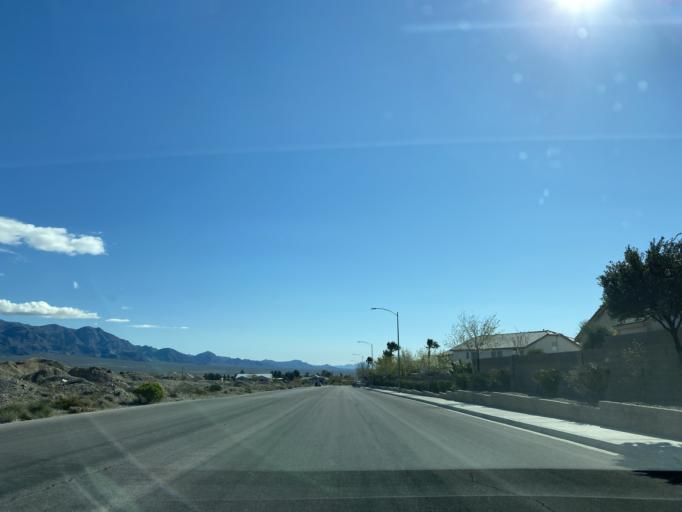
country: US
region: Nevada
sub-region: Clark County
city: Summerlin South
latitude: 36.3287
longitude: -115.2915
